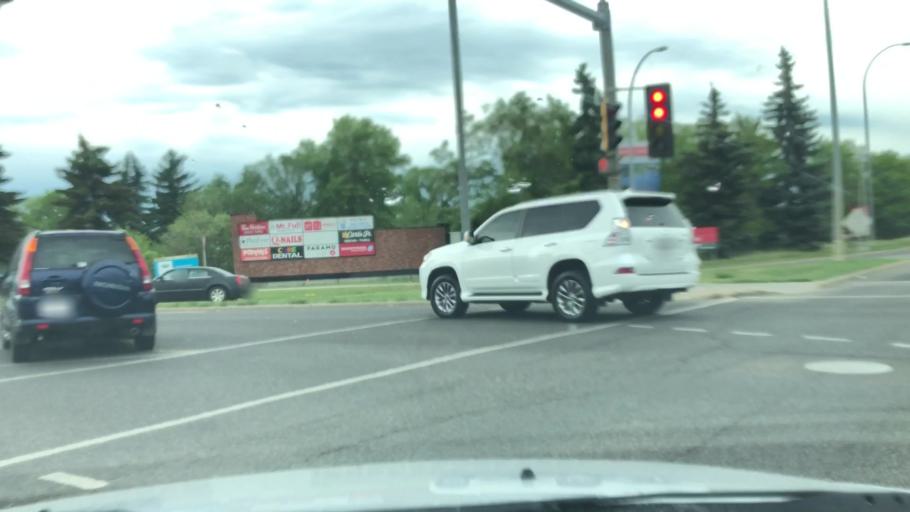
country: CA
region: Alberta
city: Edmonton
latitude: 53.5994
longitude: -113.4921
